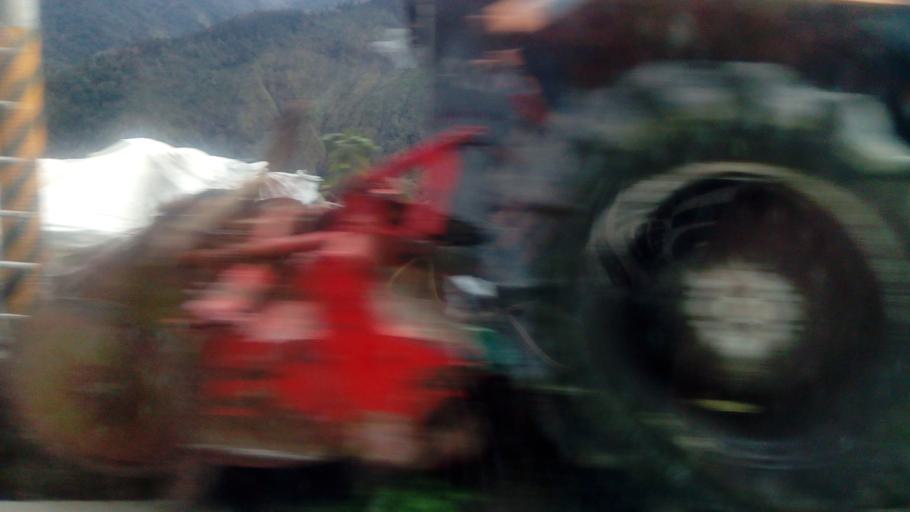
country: TW
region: Taiwan
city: Daxi
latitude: 24.4650
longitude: 121.3987
